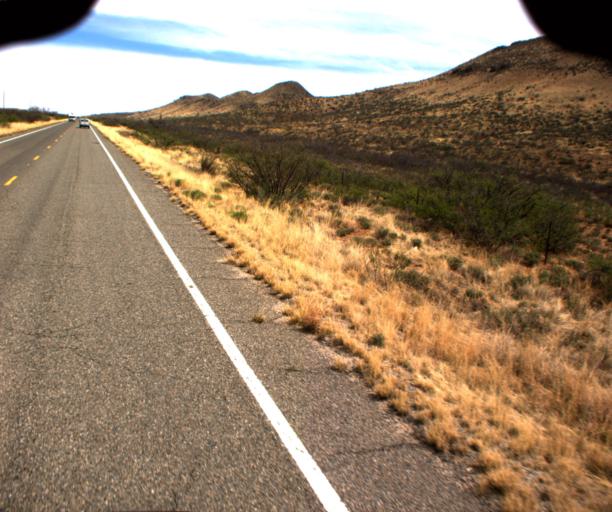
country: US
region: Arizona
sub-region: Cochise County
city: Willcox
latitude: 32.1794
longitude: -109.6323
